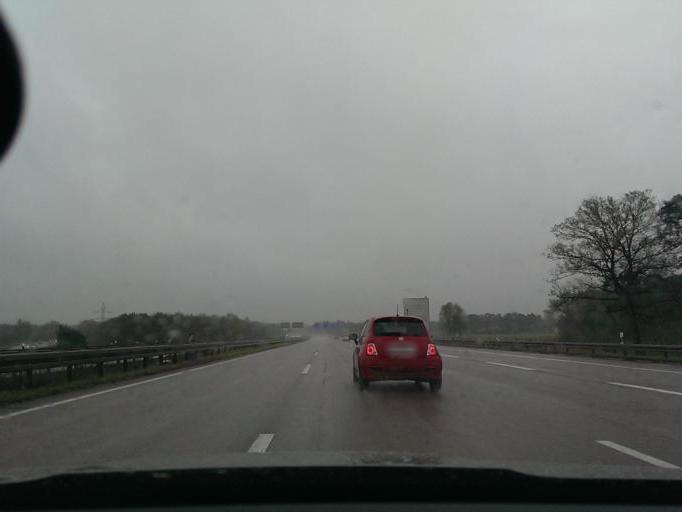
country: DE
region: Lower Saxony
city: Elze
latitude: 52.5498
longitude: 9.7953
